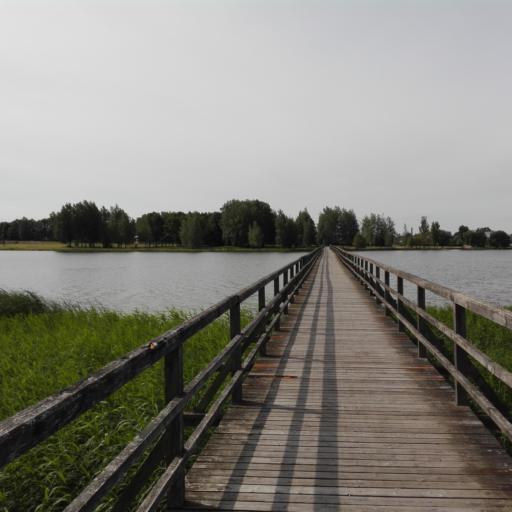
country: LT
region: Panevezys
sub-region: Birzai
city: Birzai
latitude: 56.2148
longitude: 24.7694
